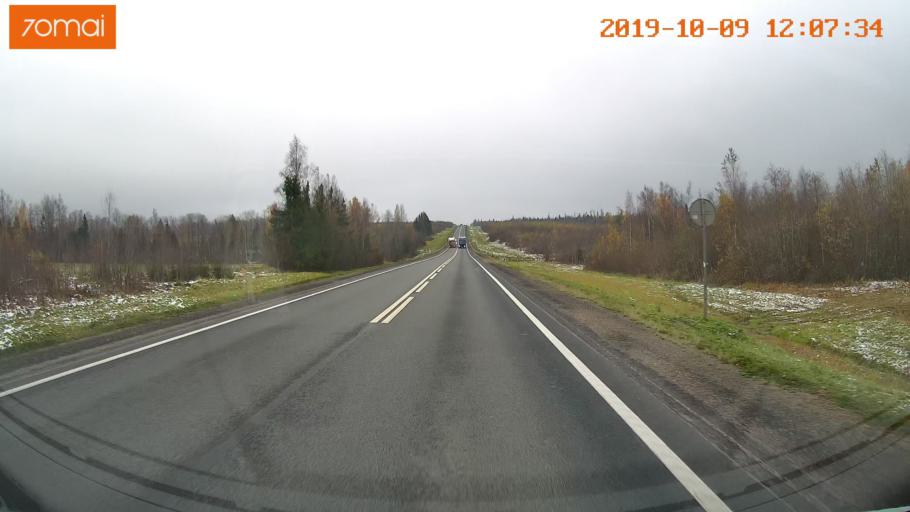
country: RU
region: Jaroslavl
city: Prechistoye
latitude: 58.5975
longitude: 40.3427
